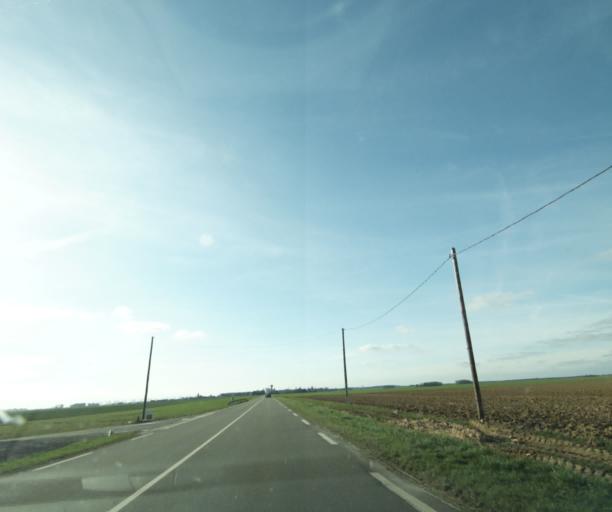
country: FR
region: Ile-de-France
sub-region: Departement de l'Essonne
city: Corbreuse
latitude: 48.4605
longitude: 1.8942
